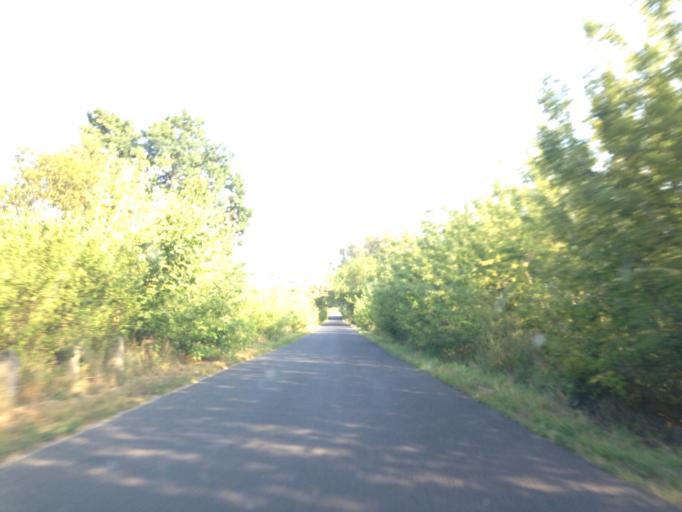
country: PL
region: Warmian-Masurian Voivodeship
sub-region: Powiat nowomiejski
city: Biskupiec
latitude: 53.4608
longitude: 19.2756
